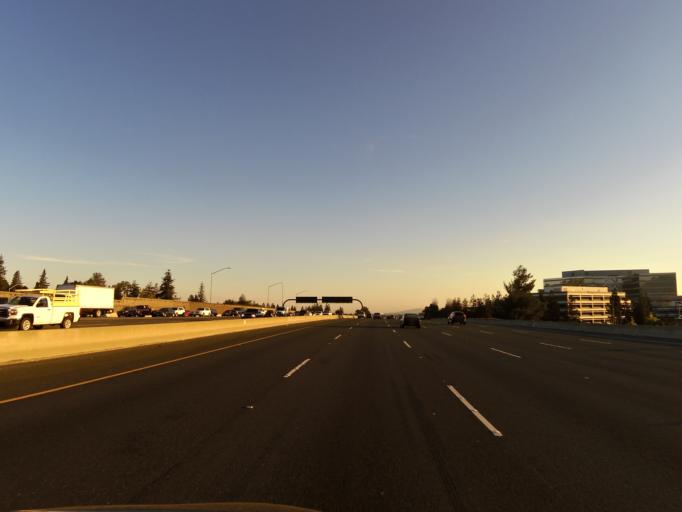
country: US
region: California
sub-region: Contra Costa County
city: Walnut Creek
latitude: 37.9058
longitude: -122.0694
